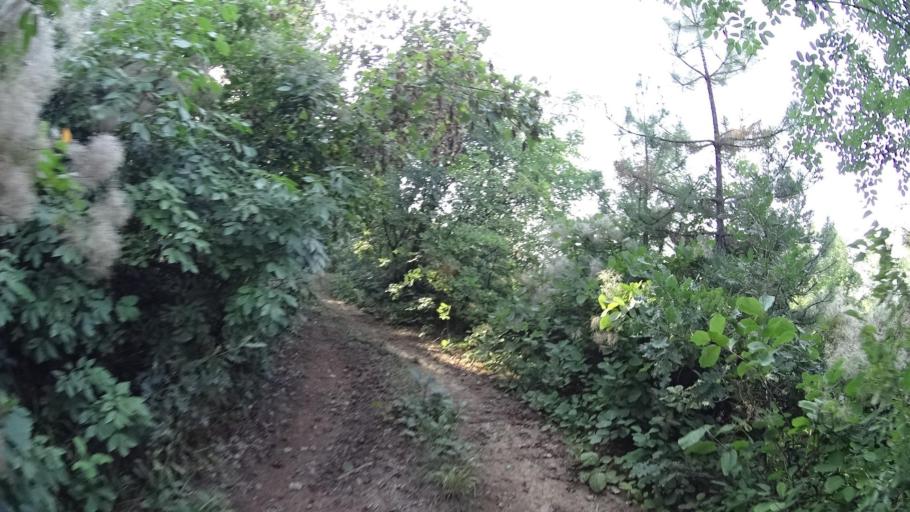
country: BG
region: Plovdiv
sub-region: Obshtina Plovdiv
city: Plovdiv
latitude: 42.0601
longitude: 24.6885
